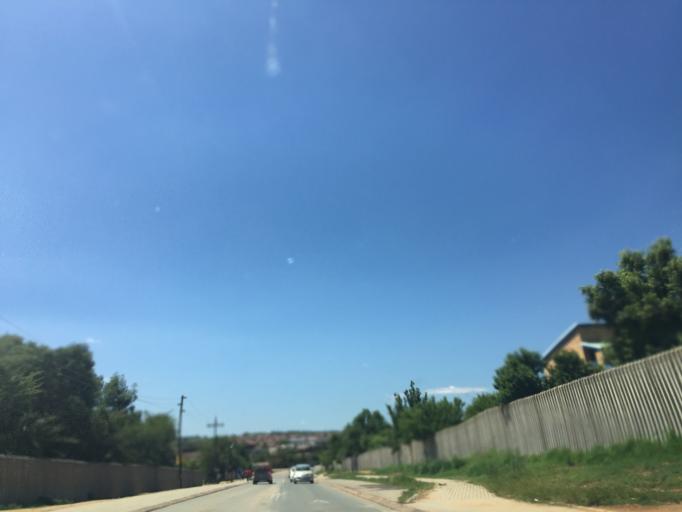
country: ZA
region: Gauteng
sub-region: West Rand District Municipality
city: Muldersdriseloop
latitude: -26.0181
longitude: 27.9288
